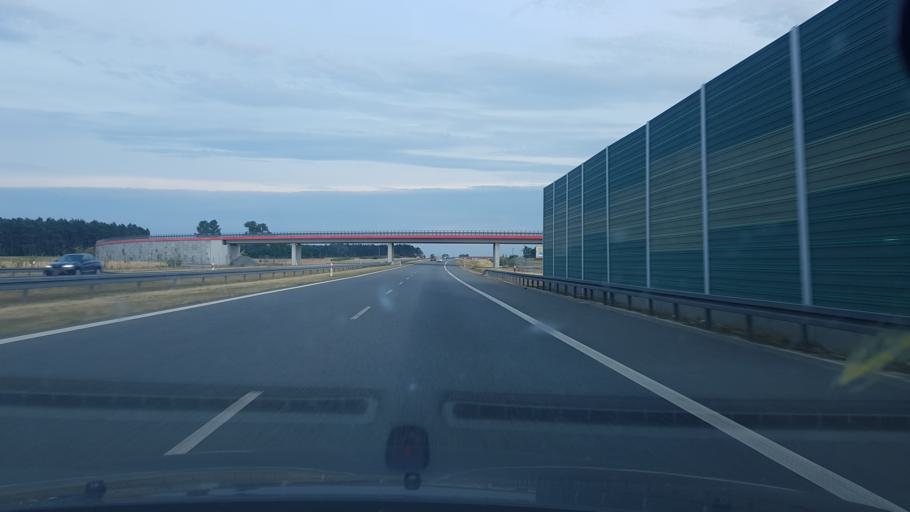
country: PL
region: Lodz Voivodeship
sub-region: Powiat kutnowski
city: Krzyzanow
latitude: 52.2018
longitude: 19.4850
